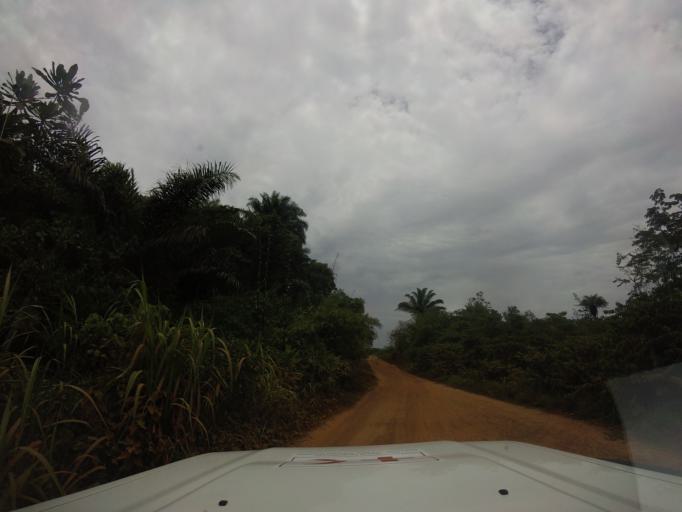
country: LR
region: Grand Cape Mount
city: Robertsport
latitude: 6.9421
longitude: -11.3273
